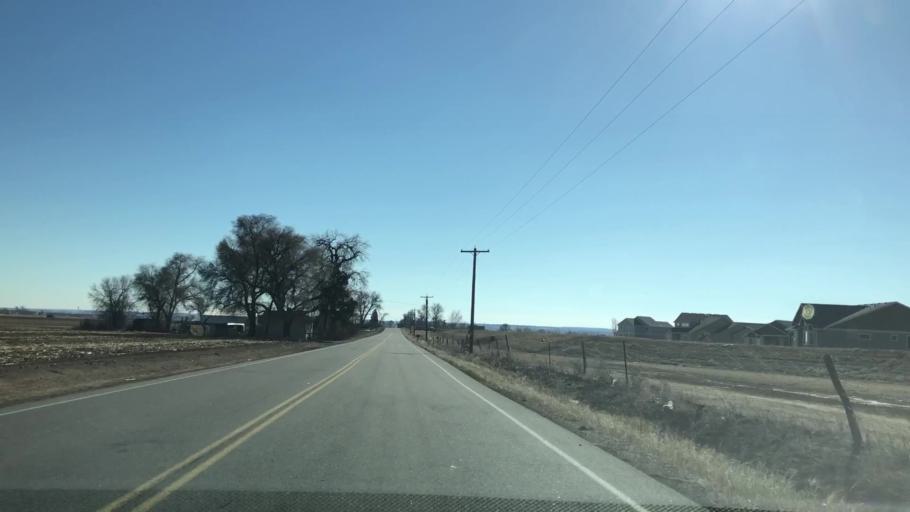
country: US
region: Colorado
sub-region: Weld County
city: Windsor
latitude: 40.5144
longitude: -104.9442
